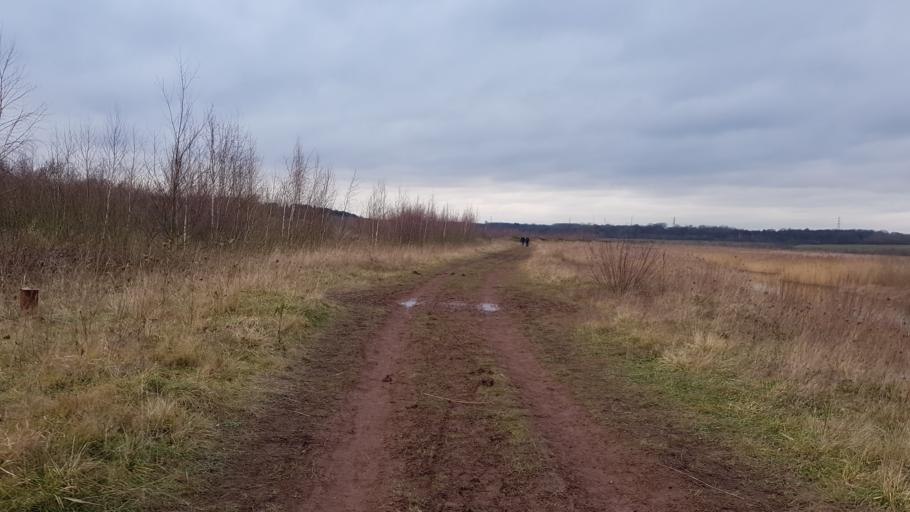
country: GB
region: England
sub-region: City and Borough of Leeds
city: Swillington
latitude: 53.7467
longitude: -1.4185
